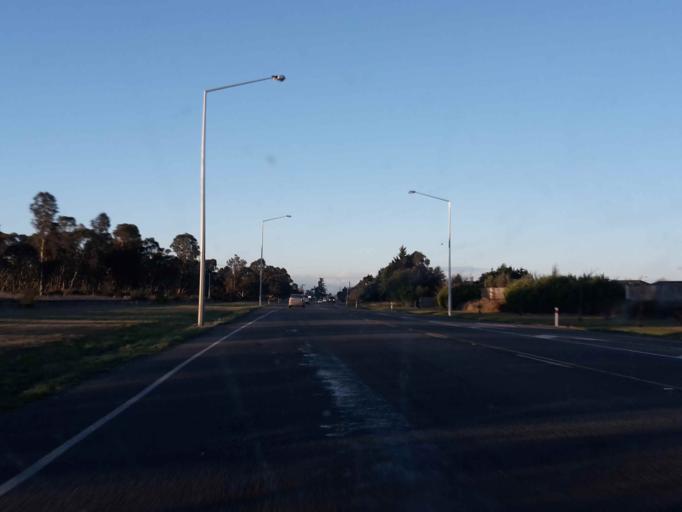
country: NZ
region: Canterbury
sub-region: Selwyn District
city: Rolleston
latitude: -43.5959
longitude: 172.3654
